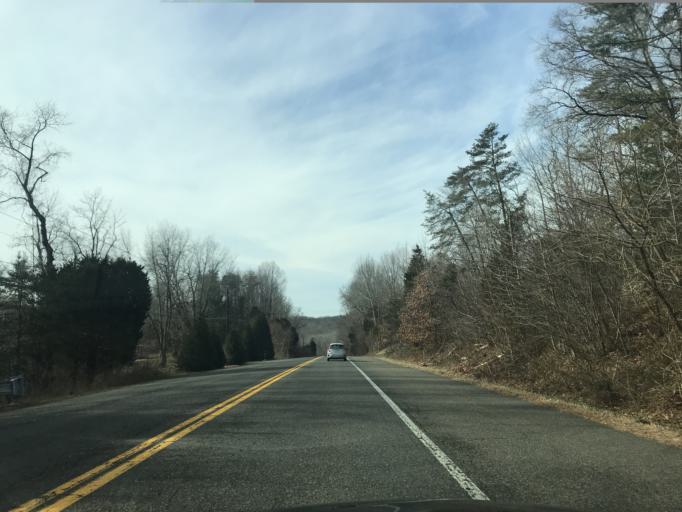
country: US
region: Maryland
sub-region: Charles County
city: La Plata
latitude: 38.4866
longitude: -77.0766
